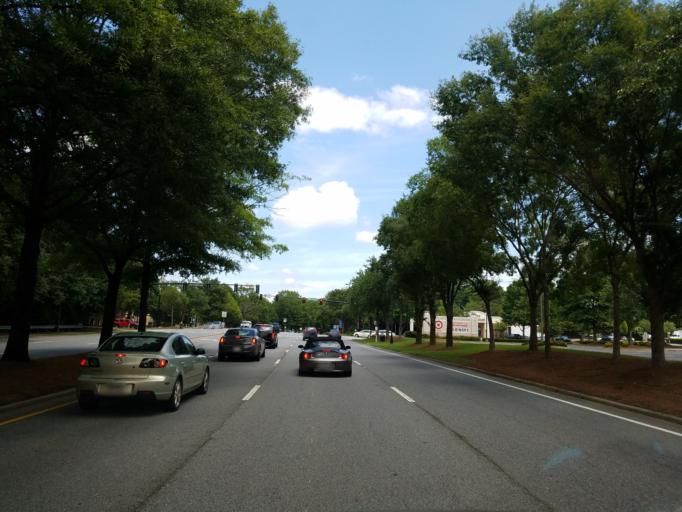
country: US
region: Georgia
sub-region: Fulton County
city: Alpharetta
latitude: 34.0473
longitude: -84.2893
